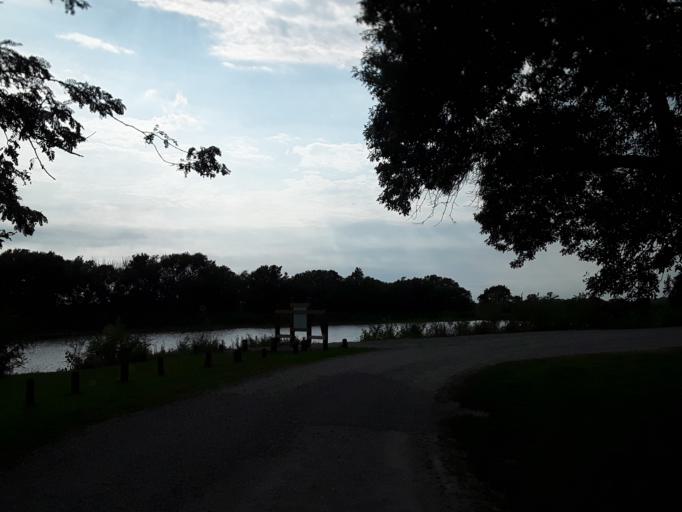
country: US
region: Nebraska
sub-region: Saunders County
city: Ashland
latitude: 41.1021
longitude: -96.4436
